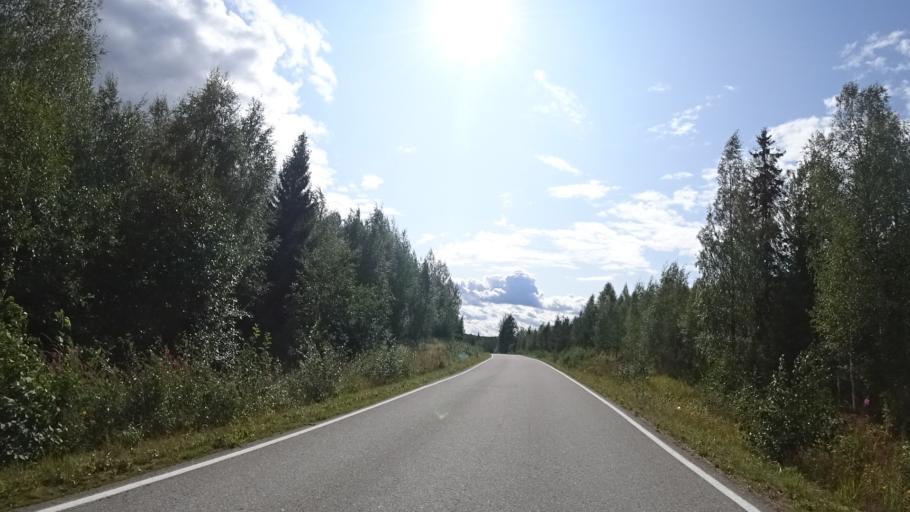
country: FI
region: North Karelia
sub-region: Joensuu
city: Ilomantsi
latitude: 62.4105
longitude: 30.9718
